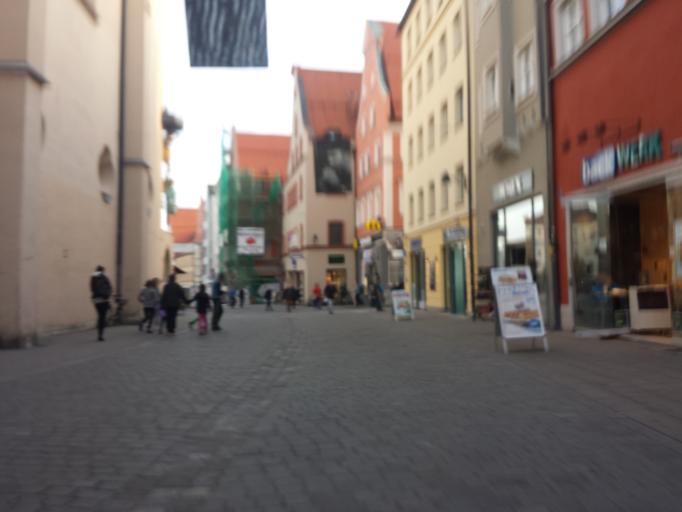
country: DE
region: Bavaria
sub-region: Upper Bavaria
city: Ingolstadt
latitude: 48.7638
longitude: 11.4243
